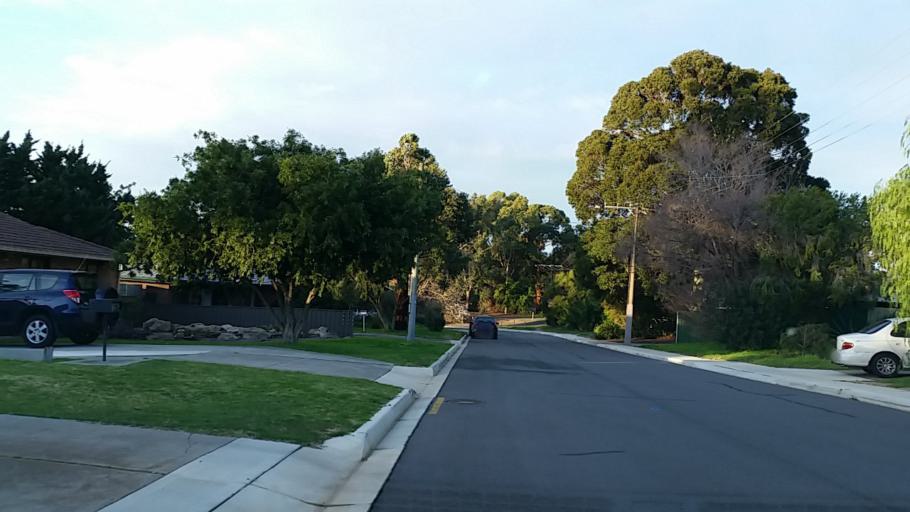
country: AU
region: South Australia
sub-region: Onkaparinga
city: Morphett Vale
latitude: -35.1354
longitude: 138.5298
